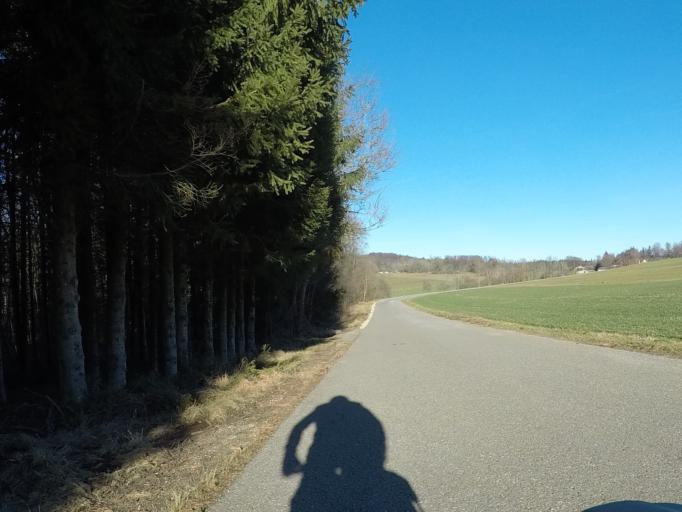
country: DE
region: Baden-Wuerttemberg
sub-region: Tuebingen Region
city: Sankt Johann
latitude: 48.4404
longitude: 9.2978
